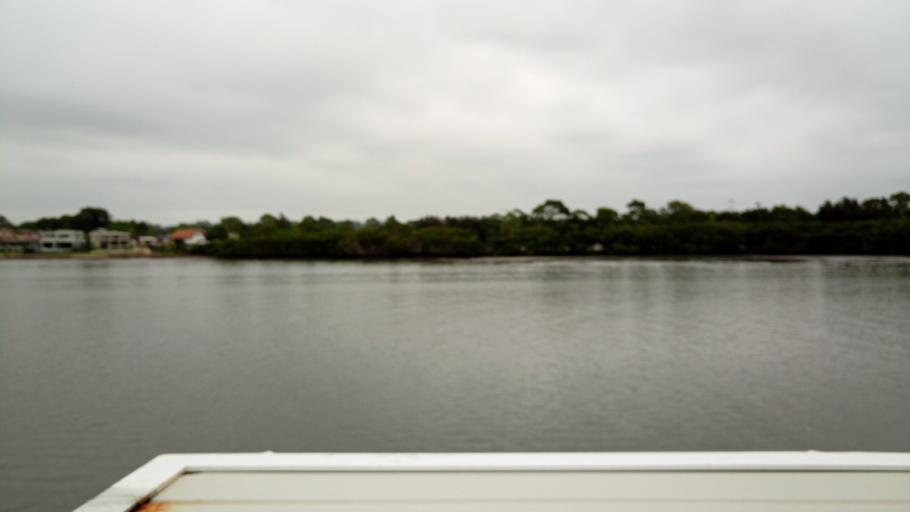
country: AU
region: New South Wales
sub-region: Canada Bay
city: Rhodes
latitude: -33.8214
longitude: 151.0824
